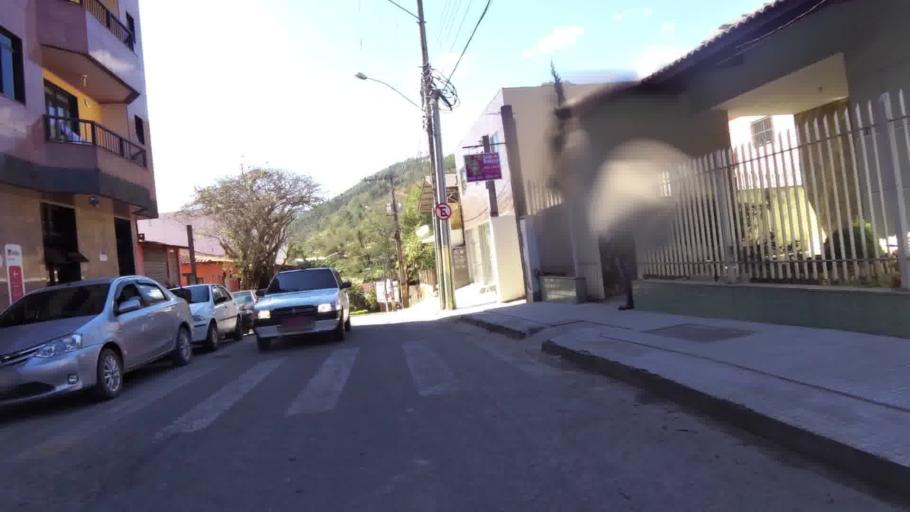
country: BR
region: Espirito Santo
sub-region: Vargem Alta
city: Vargem Alta
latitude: -20.6740
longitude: -41.0122
